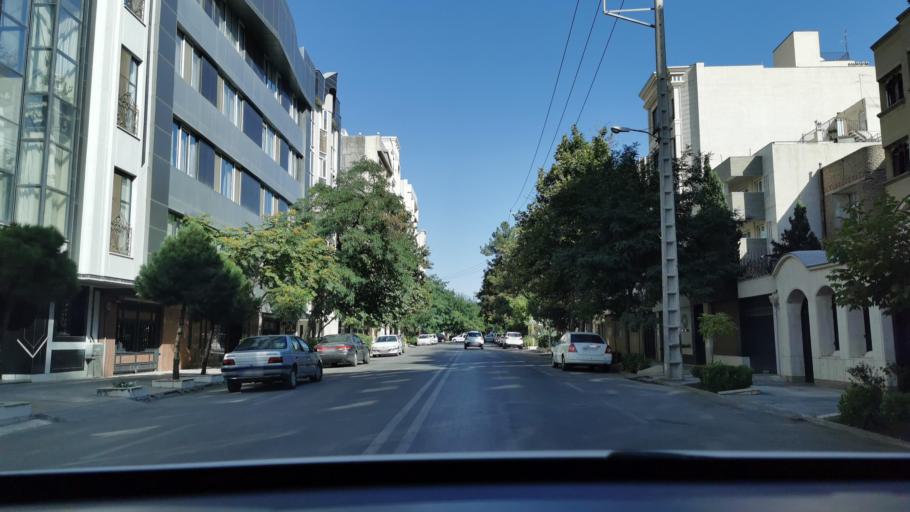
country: IR
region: Razavi Khorasan
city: Mashhad
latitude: 36.3148
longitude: 59.5480
